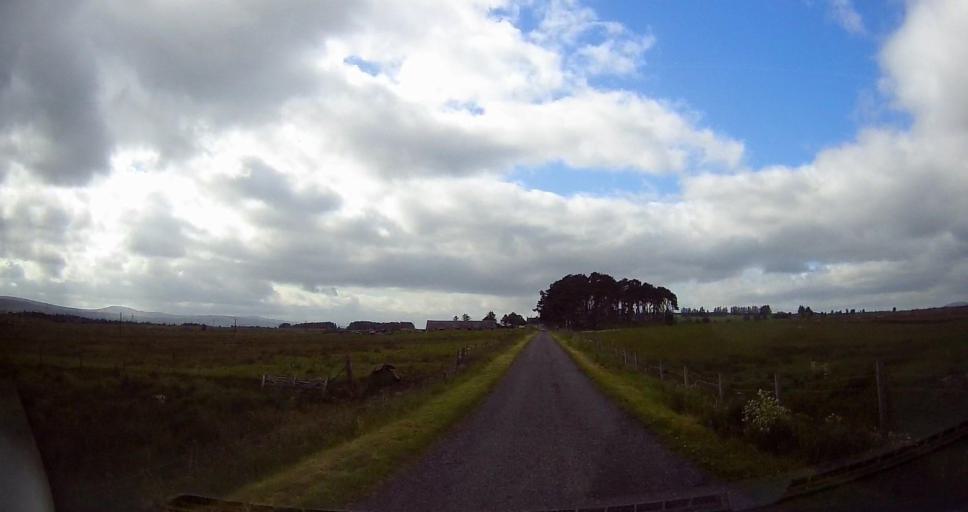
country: GB
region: Scotland
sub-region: Highland
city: Alness
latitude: 58.0695
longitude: -4.4293
